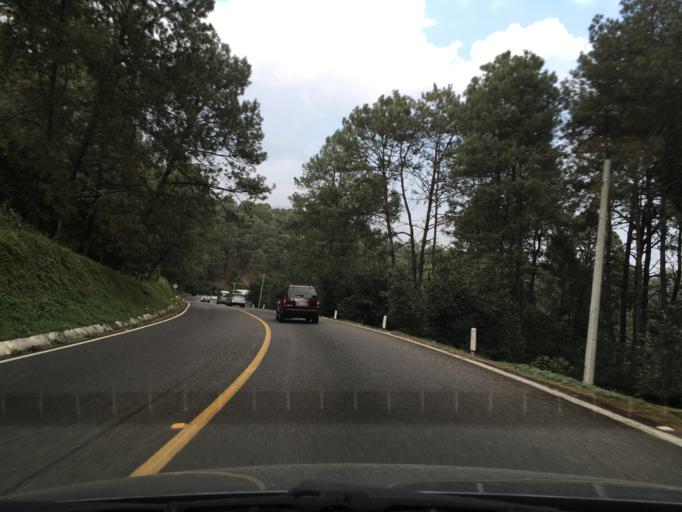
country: MX
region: Michoacan
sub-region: Uruapan
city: Toreo Bajo (El Toreo Bajo)
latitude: 19.4701
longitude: -101.9359
